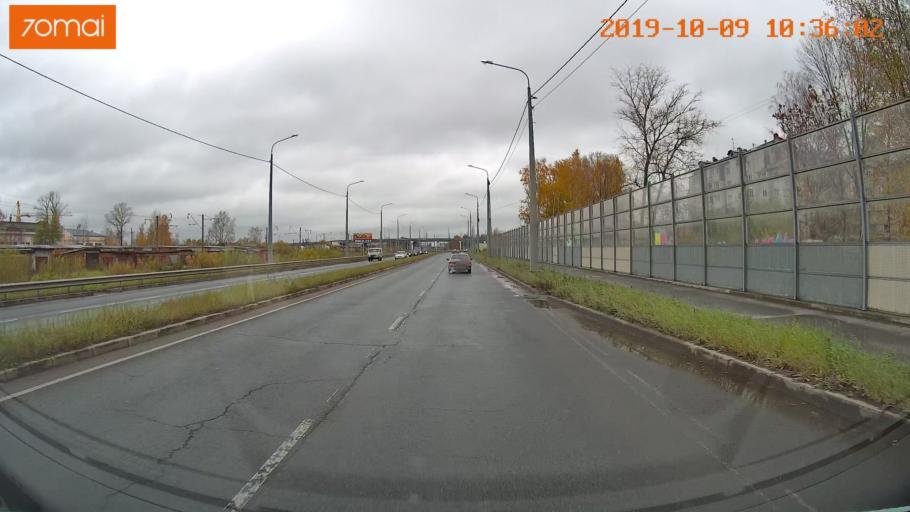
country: RU
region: Vologda
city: Vologda
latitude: 59.2302
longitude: 39.8632
